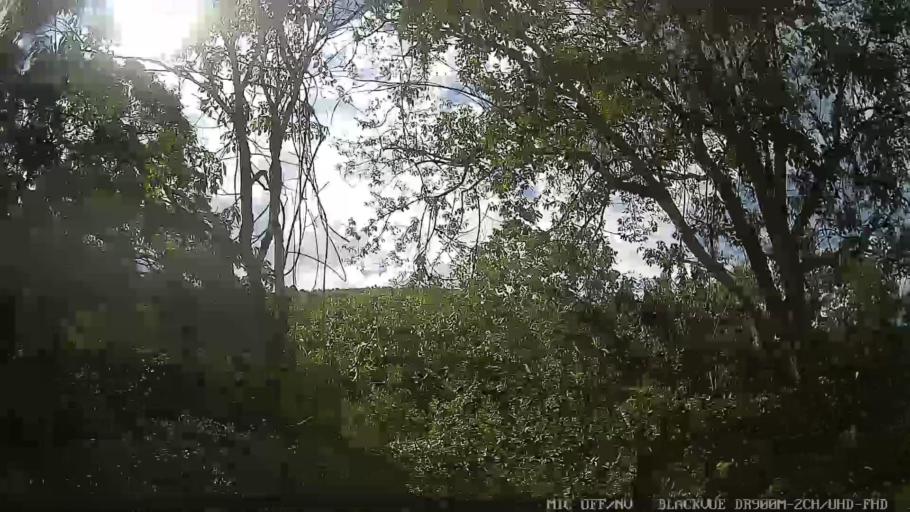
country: BR
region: Sao Paulo
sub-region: Biritiba-Mirim
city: Biritiba Mirim
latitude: -23.5368
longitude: -45.9076
